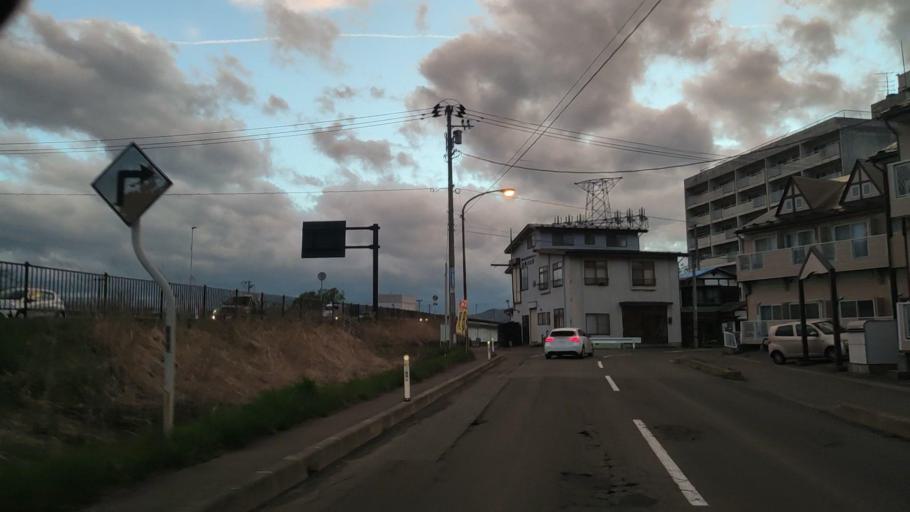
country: JP
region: Iwate
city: Morioka-shi
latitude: 39.7090
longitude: 141.1111
